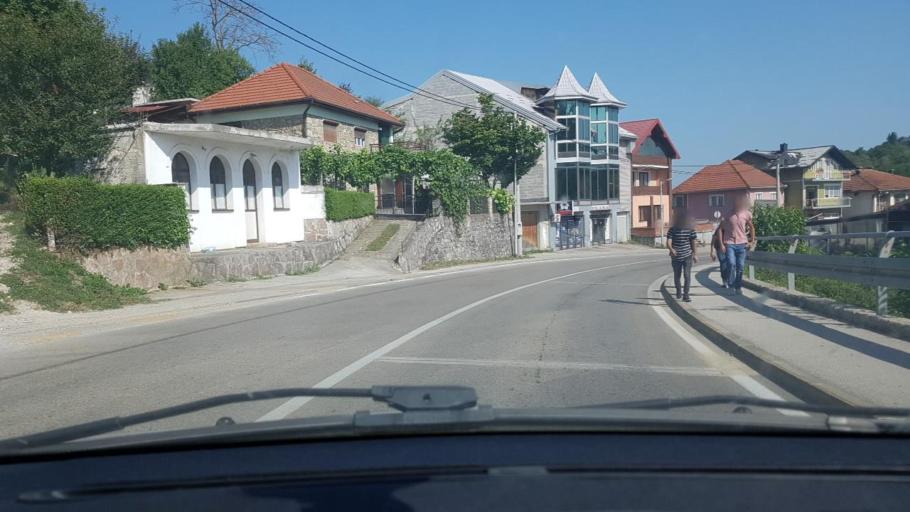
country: BA
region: Federation of Bosnia and Herzegovina
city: Pecigrad
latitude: 45.0530
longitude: 15.8963
